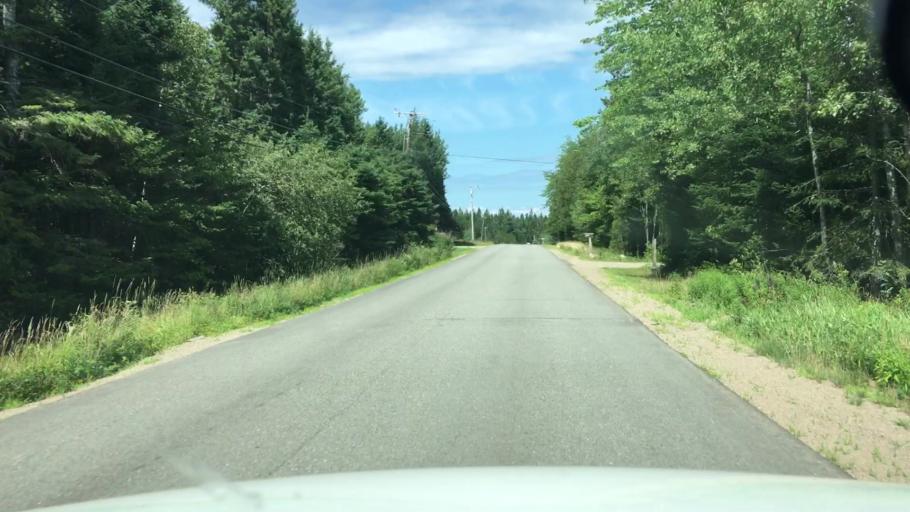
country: CA
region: New Brunswick
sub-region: Charlotte County
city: Saint Andrews
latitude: 44.9846
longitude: -67.0688
